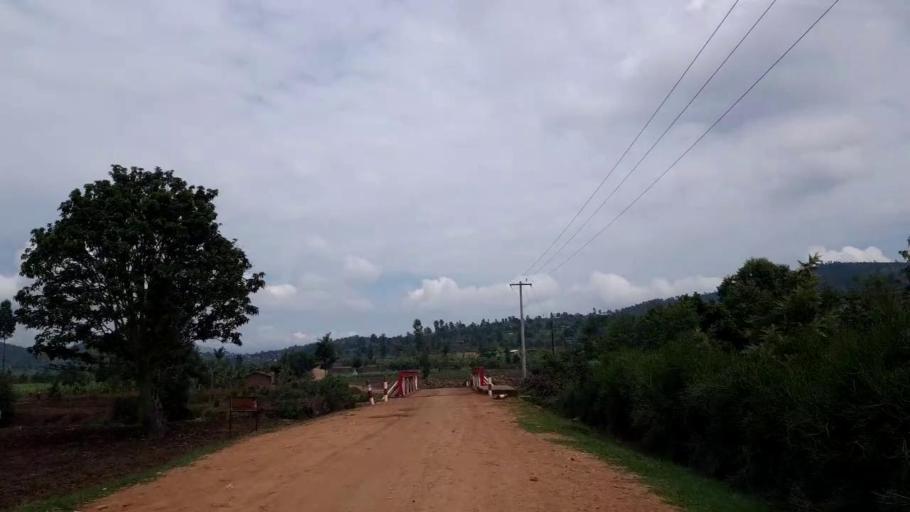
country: RW
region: Northern Province
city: Byumba
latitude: -1.4966
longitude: 30.2083
